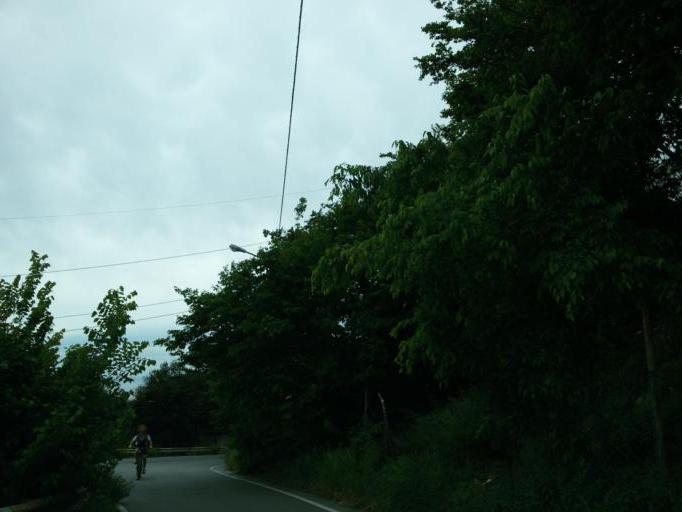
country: IT
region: Liguria
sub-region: Provincia di Genova
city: Genoa
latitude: 44.4292
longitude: 8.9113
